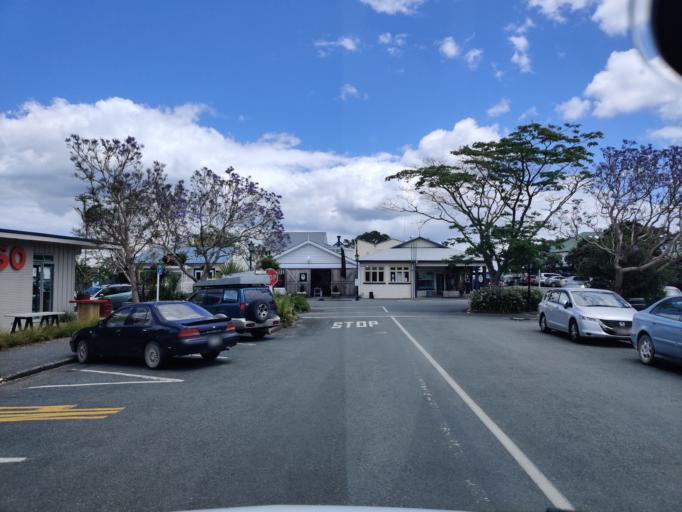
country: NZ
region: Northland
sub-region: Far North District
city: Paihia
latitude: -35.2618
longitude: 174.1227
